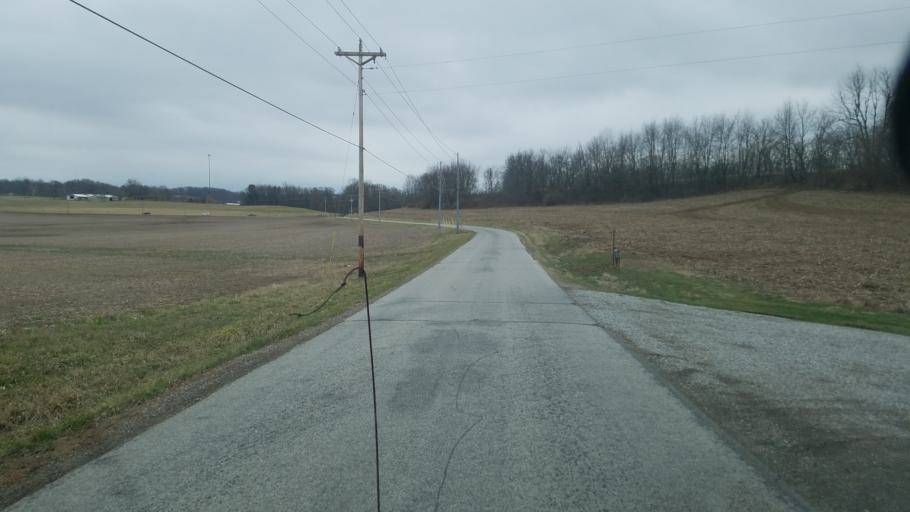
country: US
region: Ohio
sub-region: Licking County
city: Utica
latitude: 40.1944
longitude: -82.4014
